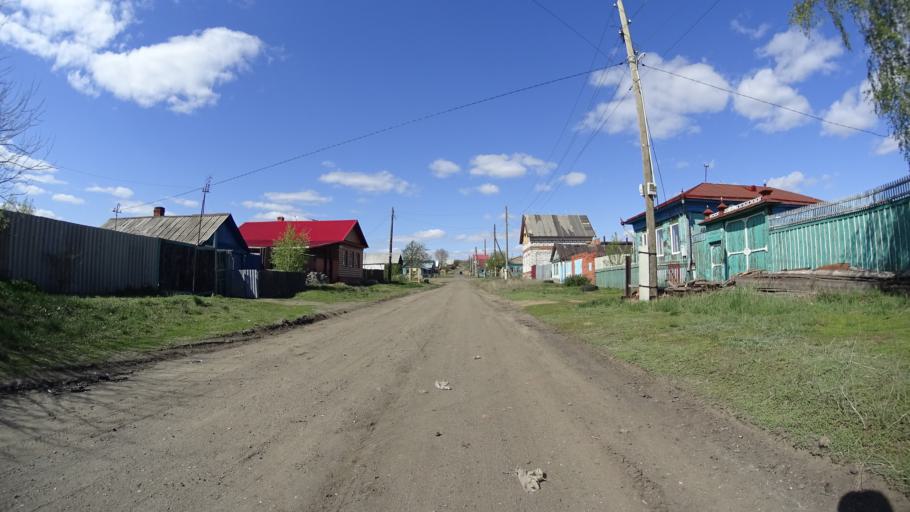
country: RU
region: Chelyabinsk
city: Troitsk
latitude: 54.0973
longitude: 61.5931
